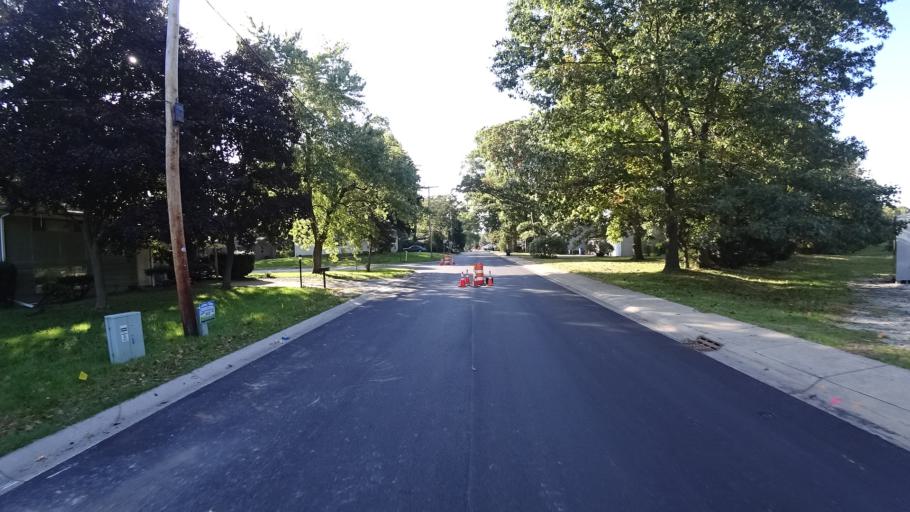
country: US
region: Indiana
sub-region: LaPorte County
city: Trail Creek
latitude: 41.7034
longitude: -86.8648
